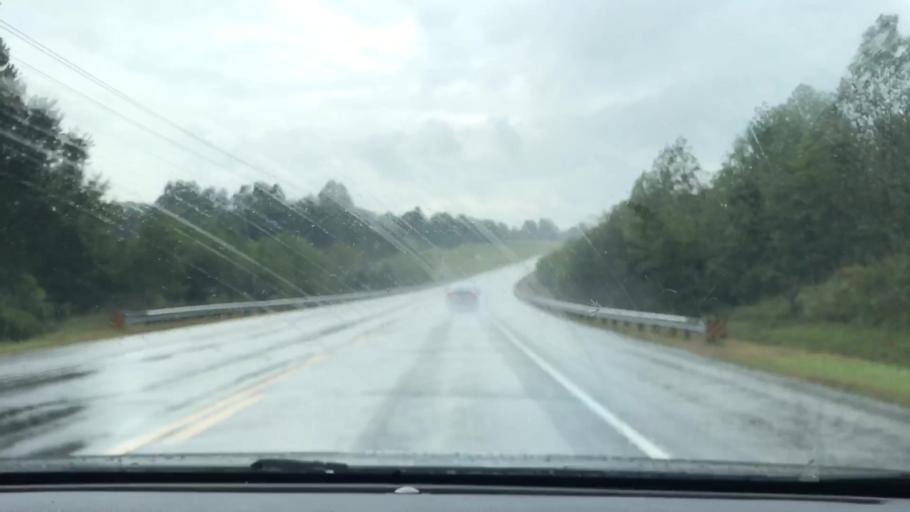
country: US
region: Tennessee
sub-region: Macon County
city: Lafayette
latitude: 36.5328
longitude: -86.0922
